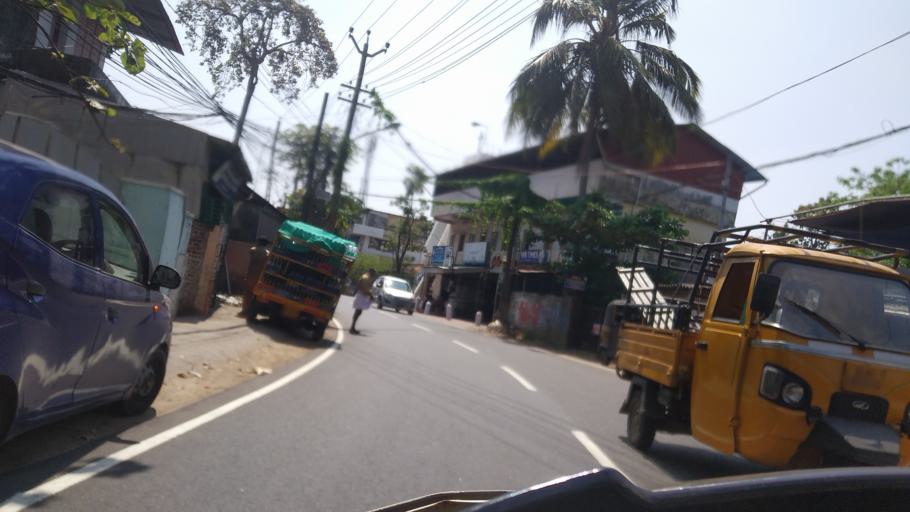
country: IN
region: Kerala
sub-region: Ernakulam
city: Cochin
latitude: 9.9934
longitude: 76.3083
